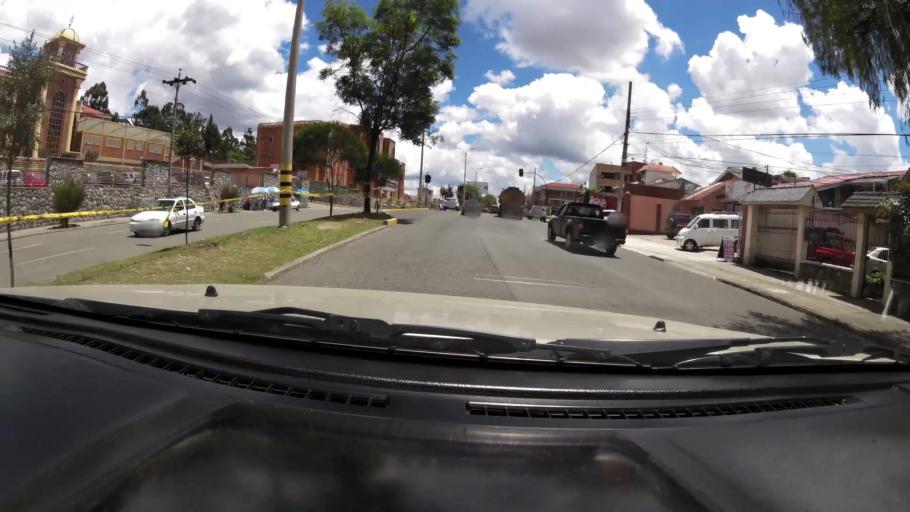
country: EC
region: Azuay
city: Cuenca
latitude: -2.8853
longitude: -79.0073
